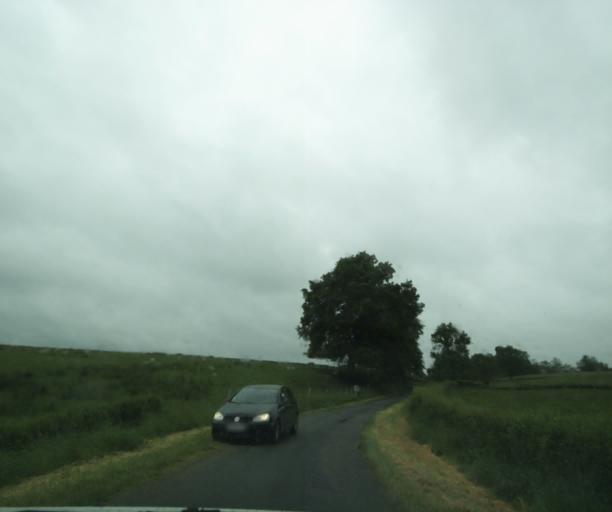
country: FR
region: Bourgogne
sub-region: Departement de Saone-et-Loire
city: Palinges
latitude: 46.4884
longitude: 4.1944
